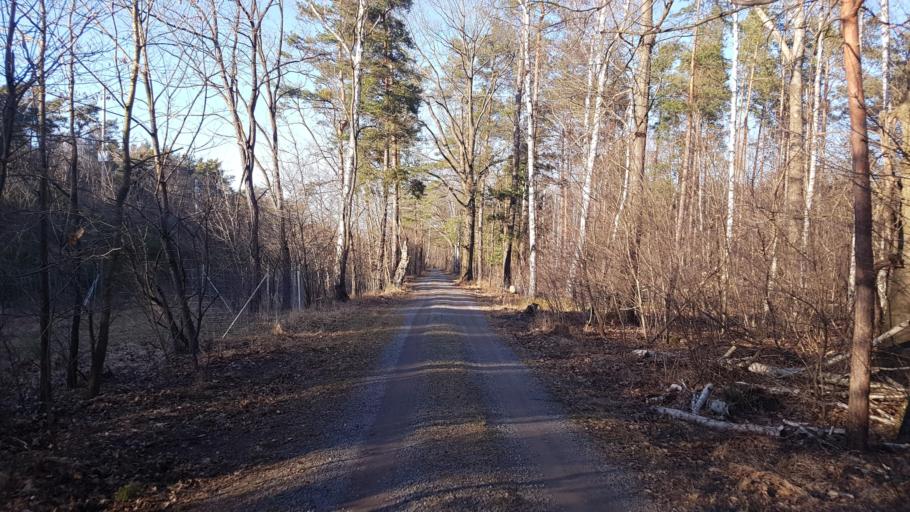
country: DE
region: Brandenburg
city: Hohenleipisch
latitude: 51.5119
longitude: 13.5768
